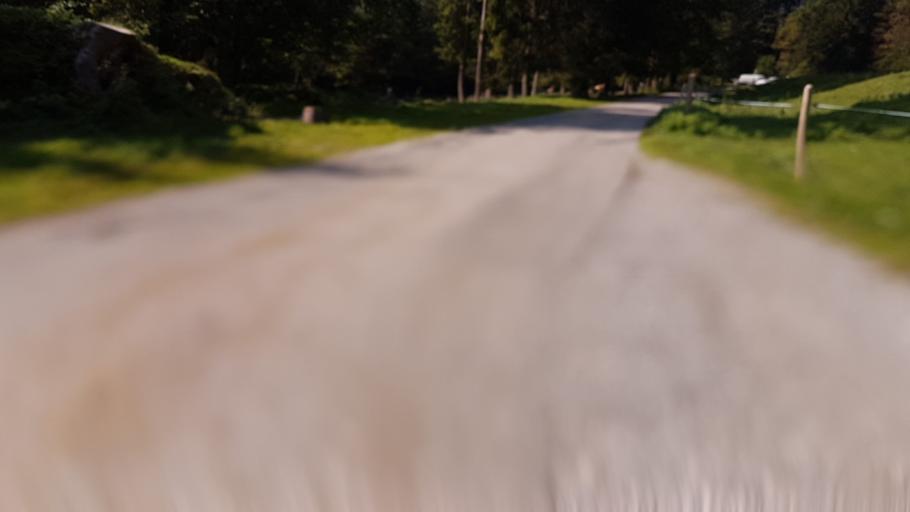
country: CH
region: Bern
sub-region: Interlaken-Oberhasli District
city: Darligen
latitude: 46.6233
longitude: 7.7598
